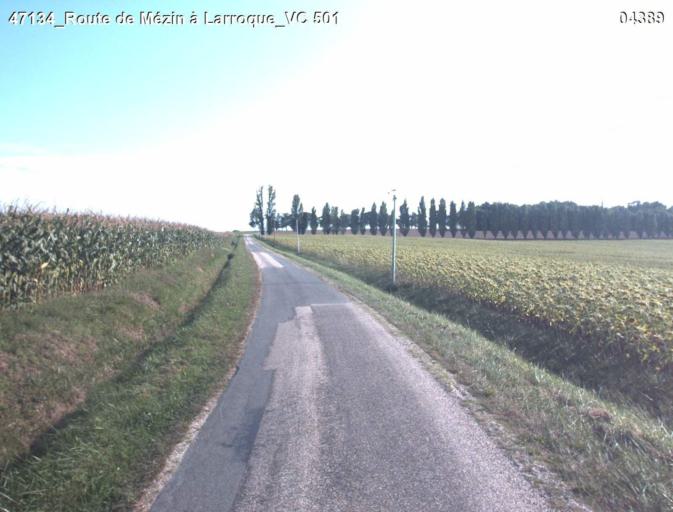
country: FR
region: Aquitaine
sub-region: Departement du Lot-et-Garonne
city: Mezin
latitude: 44.0337
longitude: 0.2675
